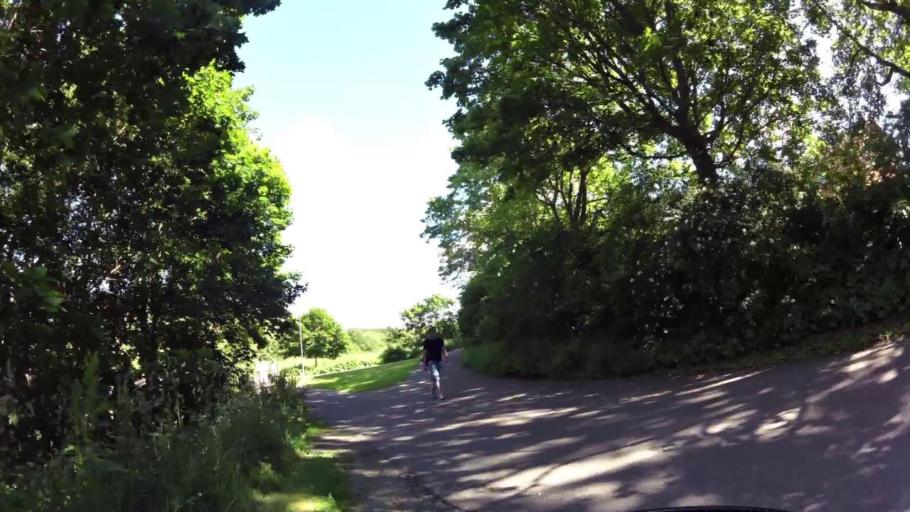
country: SE
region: OEstergoetland
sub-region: Linkopings Kommun
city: Linkoping
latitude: 58.3986
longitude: 15.6258
